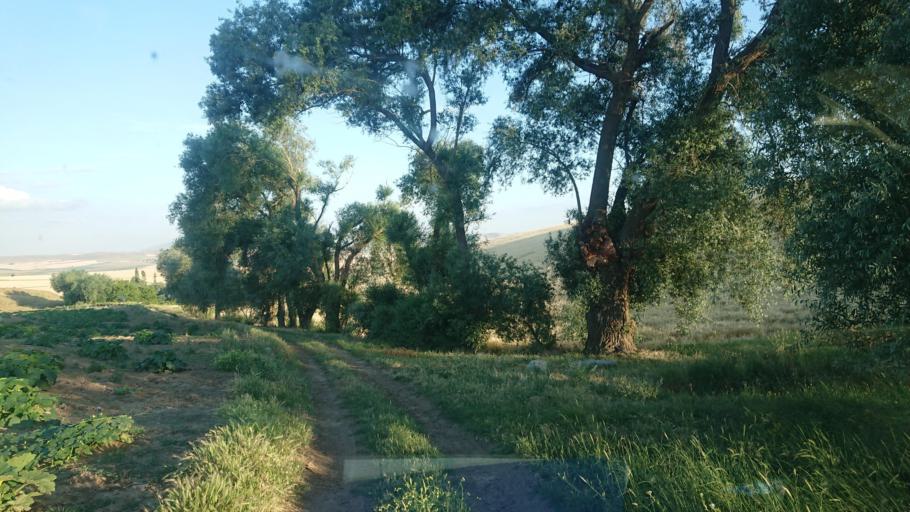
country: TR
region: Aksaray
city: Agacoren
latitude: 38.8325
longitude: 33.8845
